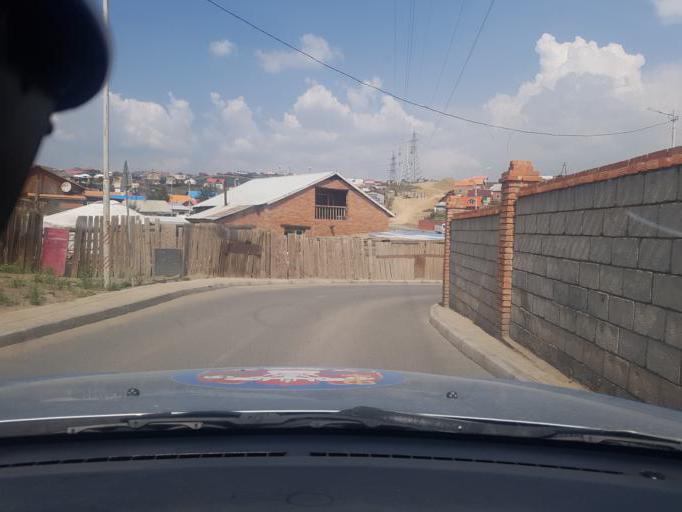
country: MN
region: Ulaanbaatar
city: Ulaanbaatar
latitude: 47.9387
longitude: 106.8976
